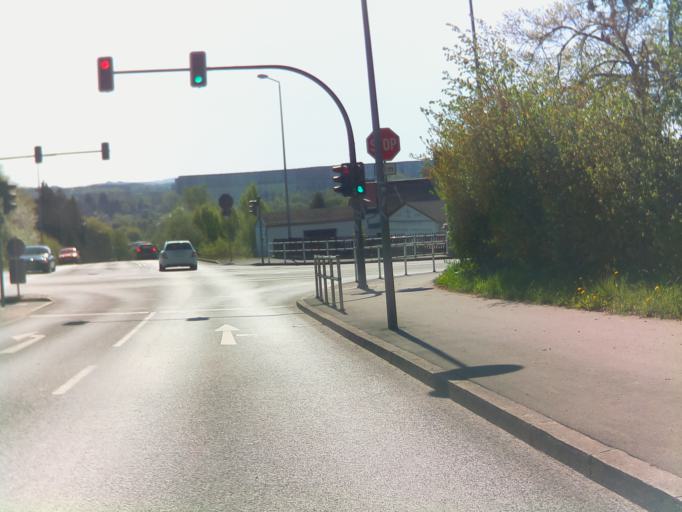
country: DE
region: Saxony
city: Plauen
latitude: 50.5070
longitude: 12.1471
